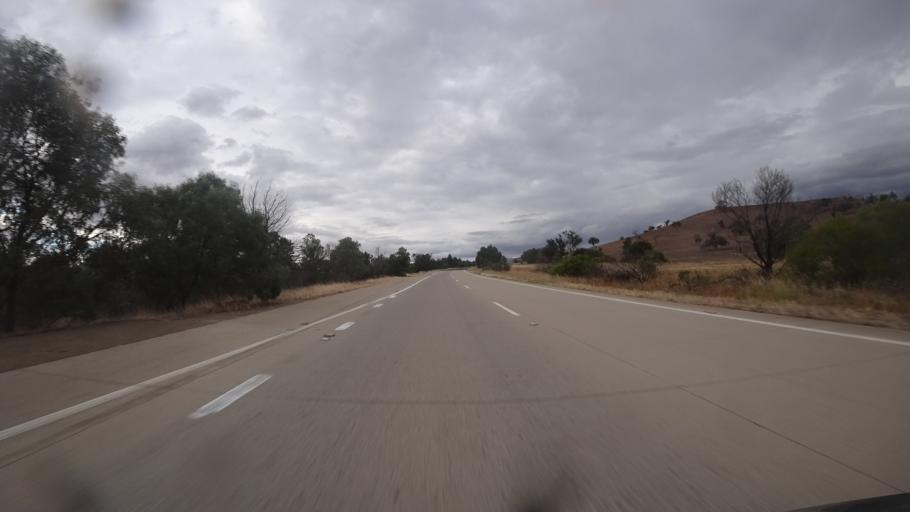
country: AU
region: New South Wales
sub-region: Yass Valley
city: Yass
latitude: -34.7927
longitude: 148.6962
